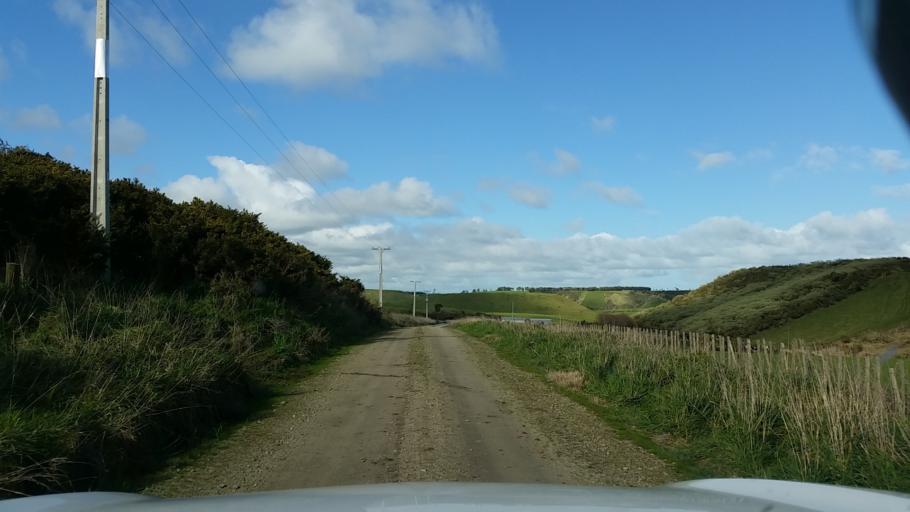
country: NZ
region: Taranaki
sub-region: South Taranaki District
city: Patea
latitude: -39.7192
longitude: 174.4696
